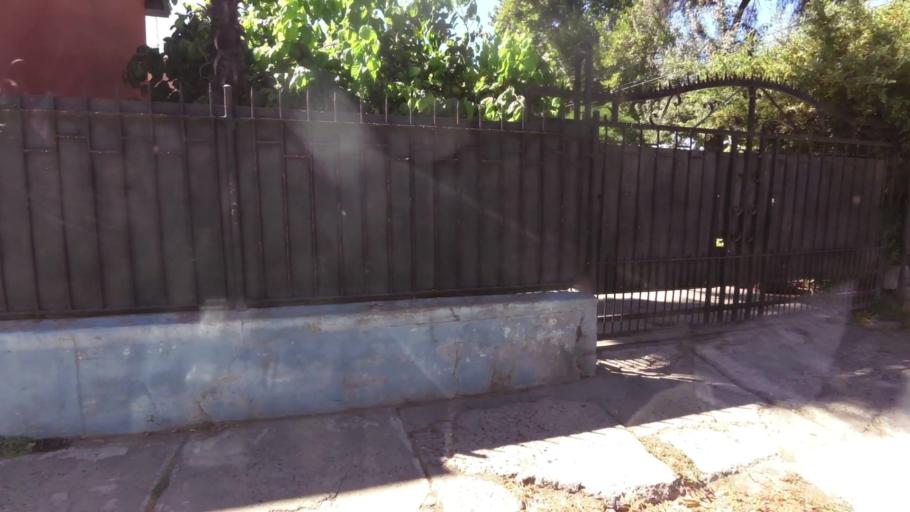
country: CL
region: O'Higgins
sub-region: Provincia de Cachapoal
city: Rancagua
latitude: -34.1773
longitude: -70.7321
